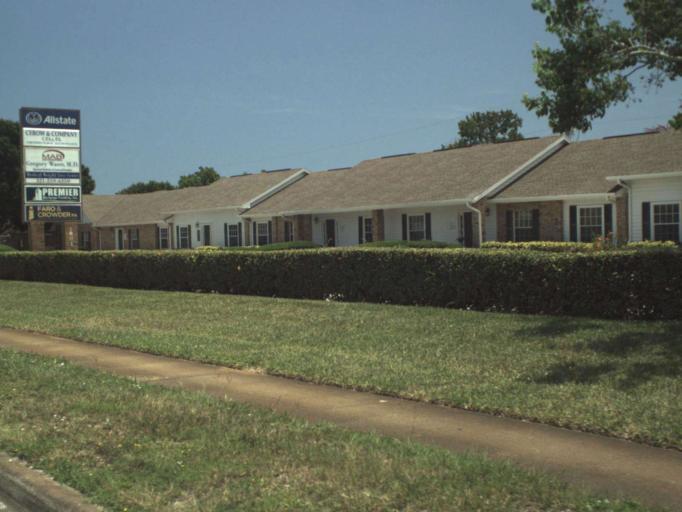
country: US
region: Florida
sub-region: Brevard County
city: West Melbourne
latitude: 28.1216
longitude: -80.6503
